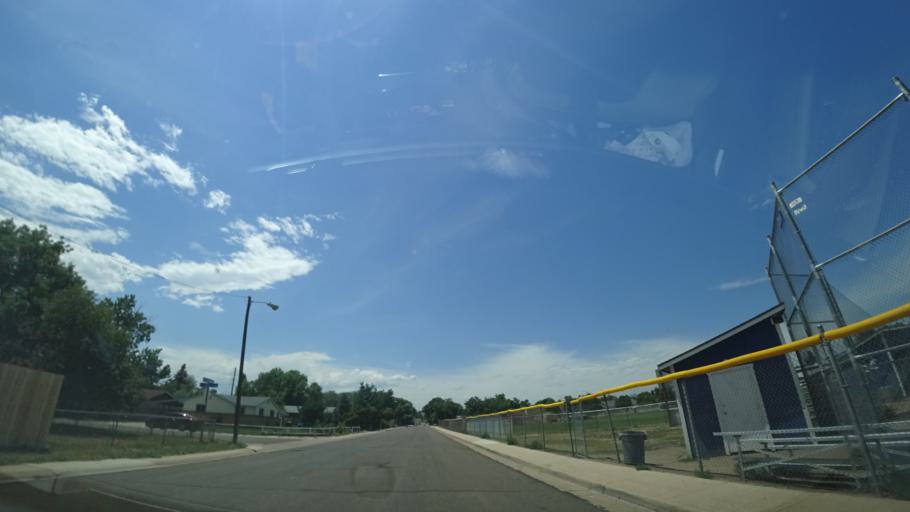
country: US
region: Colorado
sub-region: Jefferson County
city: Lakewood
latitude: 39.6921
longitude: -105.0840
